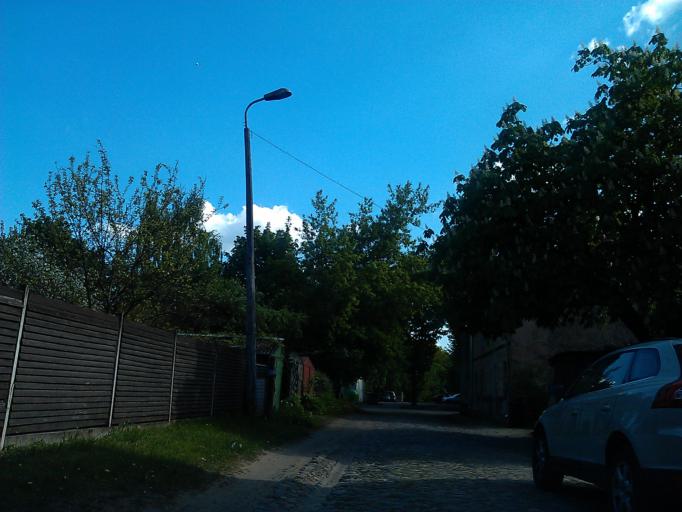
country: LV
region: Riga
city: Jaunciems
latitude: 56.9858
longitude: 24.1834
